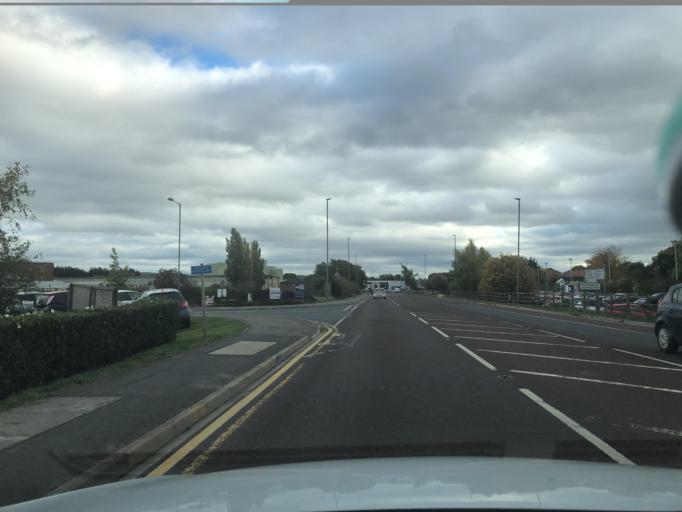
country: GB
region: England
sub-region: North Yorkshire
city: Northallerton
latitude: 54.3497
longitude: -1.4441
